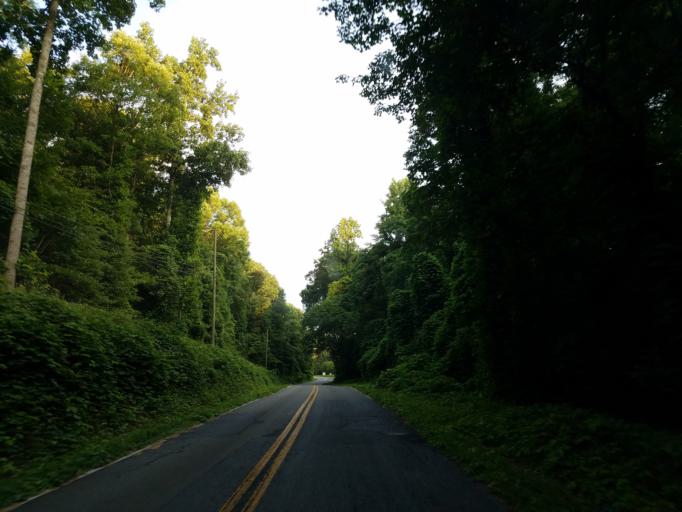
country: US
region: Georgia
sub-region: Pickens County
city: Jasper
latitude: 34.4763
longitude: -84.4171
